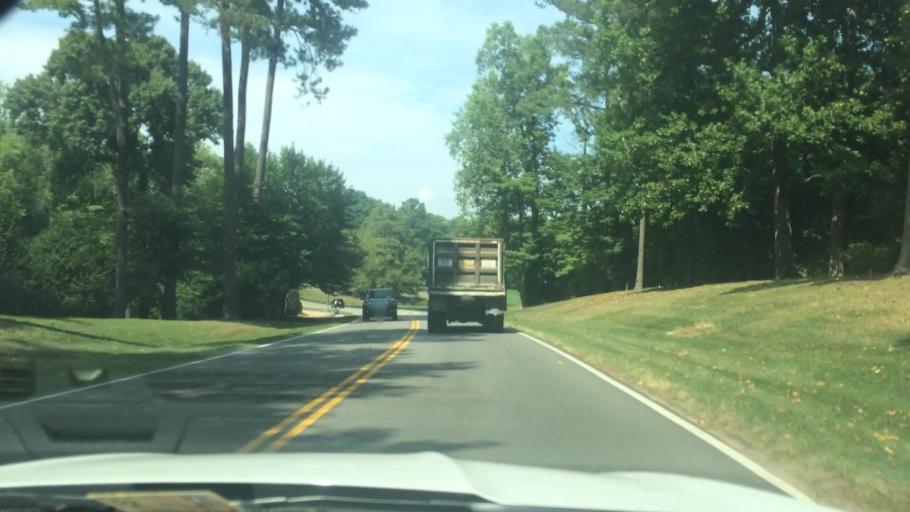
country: US
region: Virginia
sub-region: City of Williamsburg
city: Williamsburg
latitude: 37.2334
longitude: -76.6606
